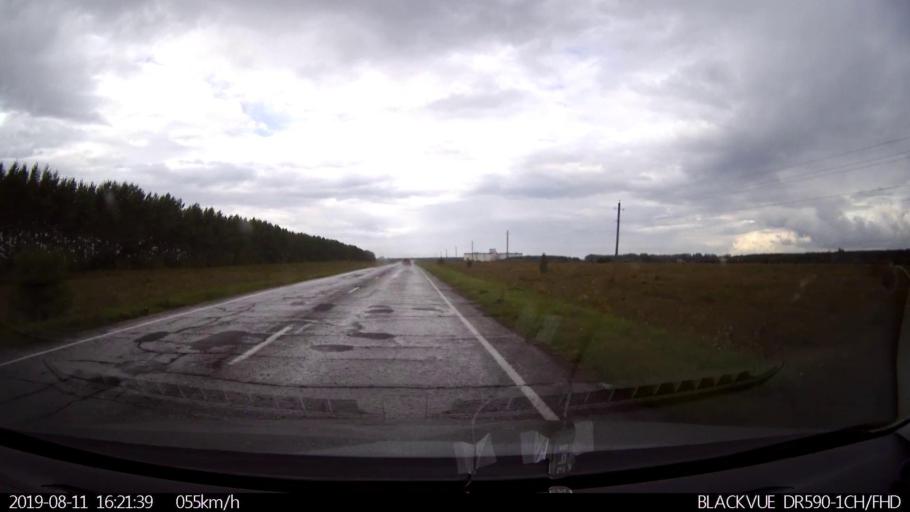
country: RU
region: Ulyanovsk
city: Mayna
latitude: 54.0815
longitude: 47.5970
